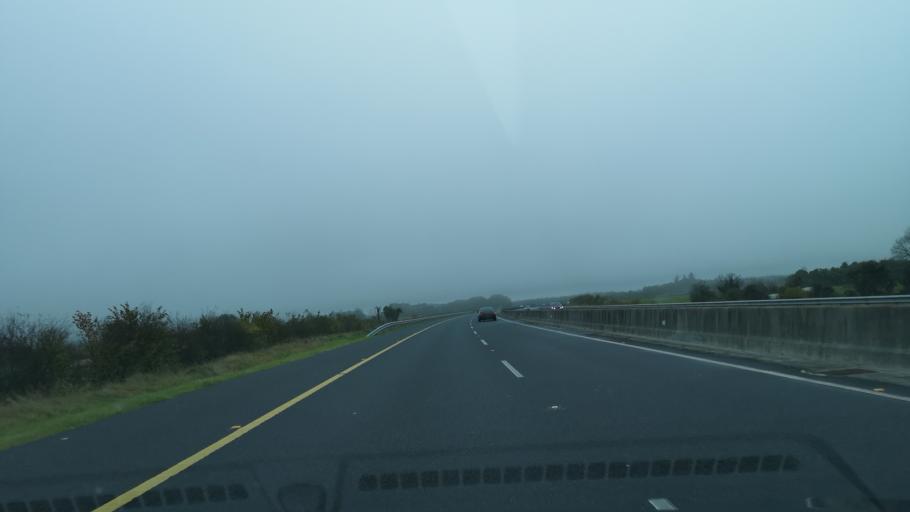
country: IE
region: Connaught
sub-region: County Galway
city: Ballinasloe
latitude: 53.2962
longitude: -8.3489
